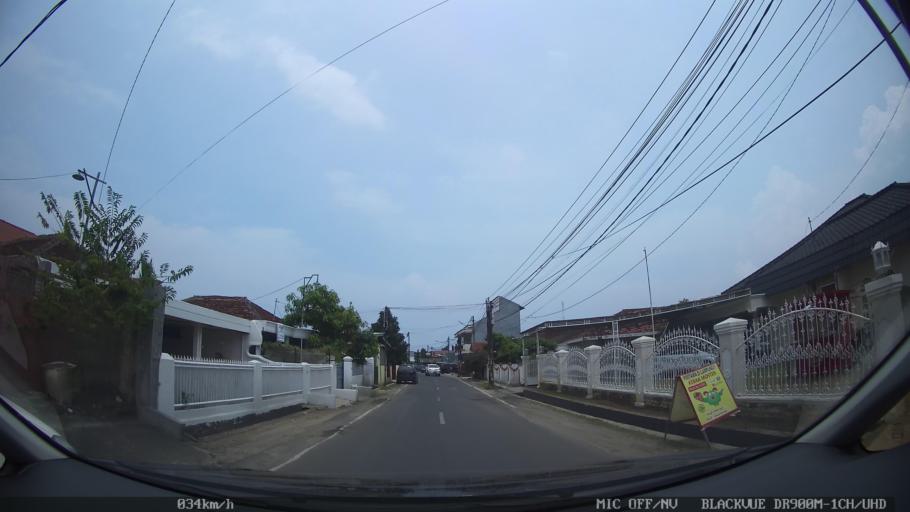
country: ID
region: Lampung
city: Bandarlampung
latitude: -5.4173
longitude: 105.2737
